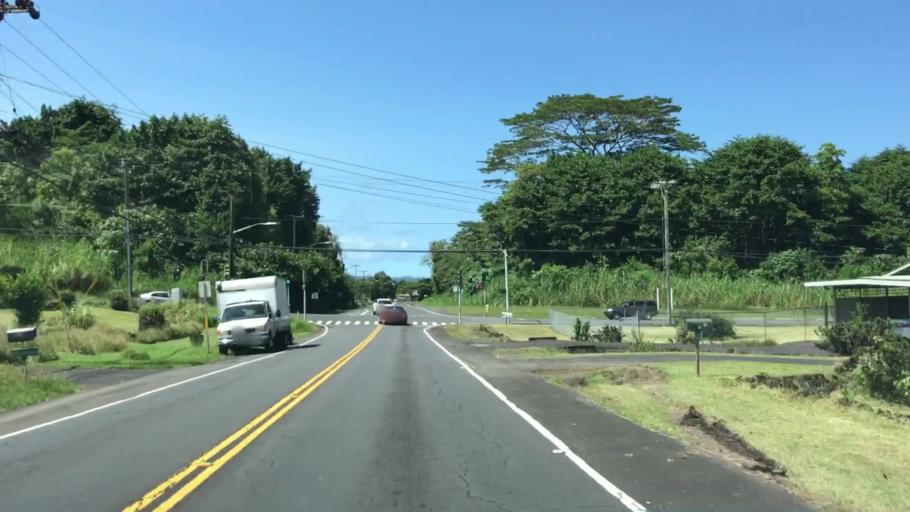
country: US
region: Hawaii
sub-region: Hawaii County
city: Hilo
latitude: 19.6933
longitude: -155.0812
